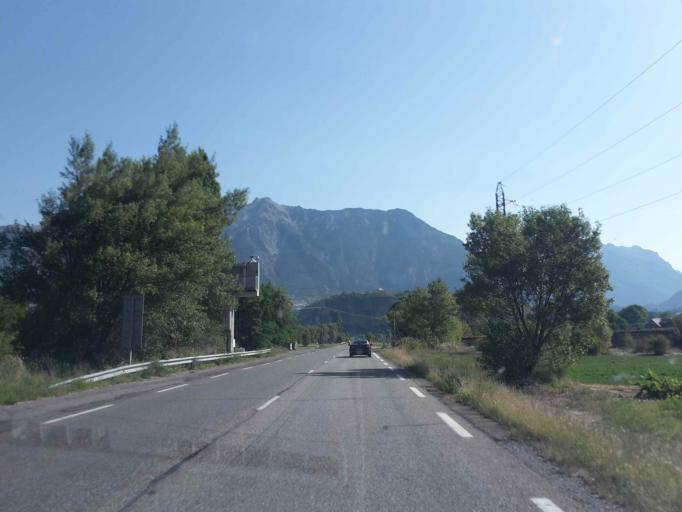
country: FR
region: Provence-Alpes-Cote d'Azur
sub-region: Departement des Hautes-Alpes
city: Guillestre
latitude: 44.6593
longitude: 6.6023
